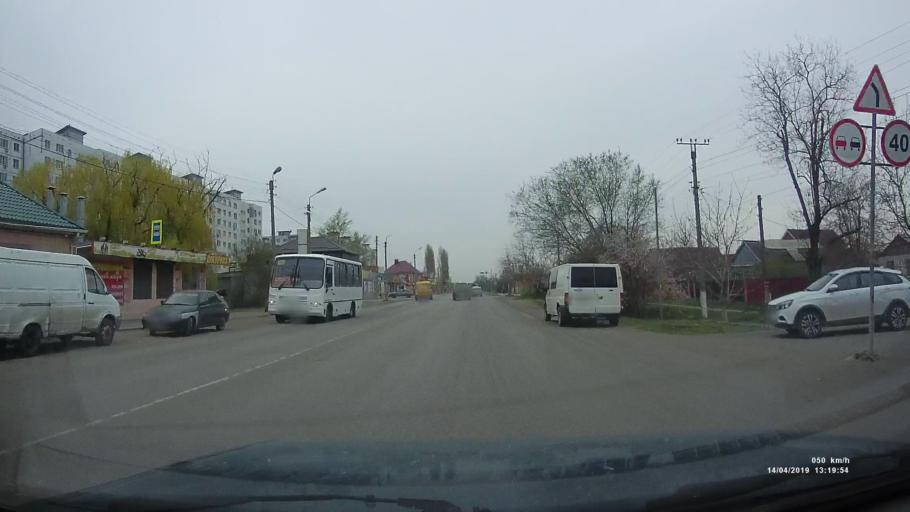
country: RU
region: Rostov
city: Kuleshovka
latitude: 47.0819
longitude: 39.5395
